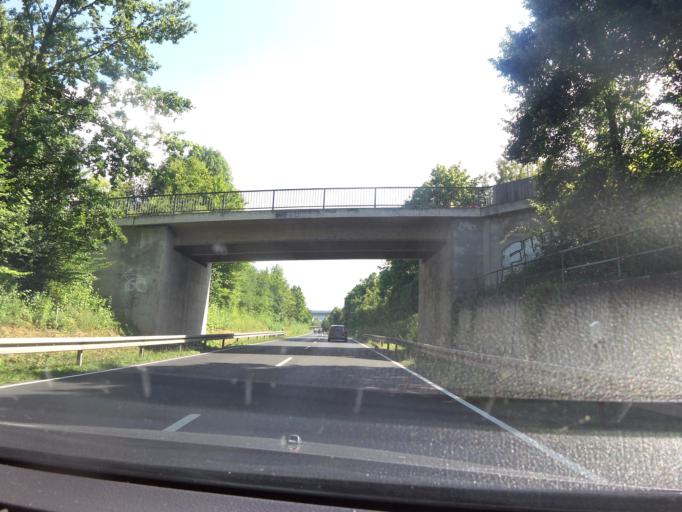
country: DE
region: Bavaria
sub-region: Regierungsbezirk Unterfranken
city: Margetshochheim
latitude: 49.8345
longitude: 9.8621
